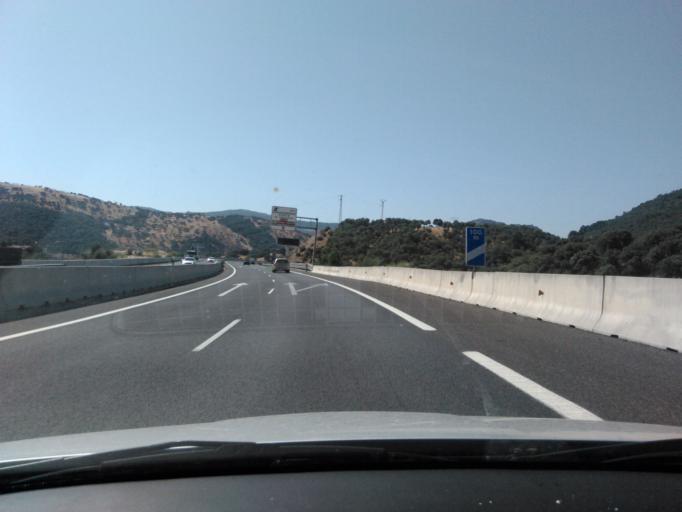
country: ES
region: Andalusia
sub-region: Provincia de Jaen
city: Santa Elena
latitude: 38.4183
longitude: -3.5006
